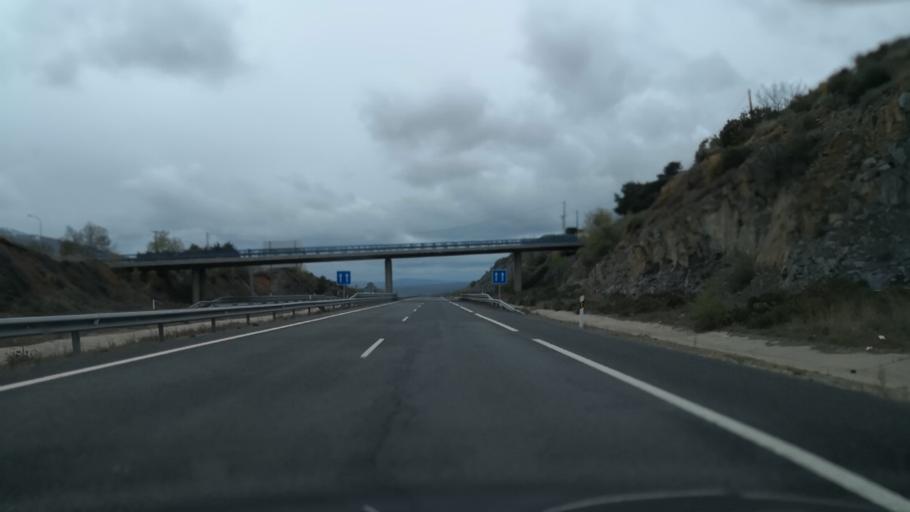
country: ES
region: Castille and Leon
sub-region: Provincia de Salamanca
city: Bejar
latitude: 40.3976
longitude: -5.7424
